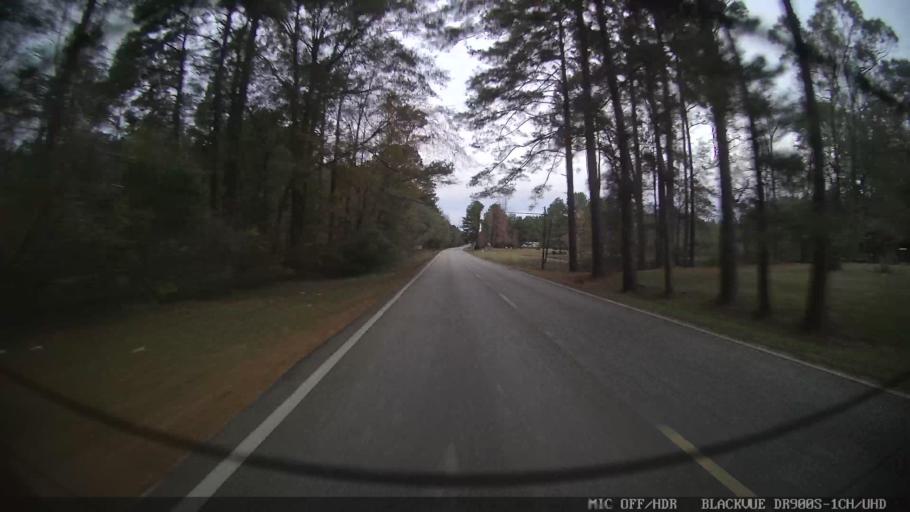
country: US
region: Mississippi
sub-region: Clarke County
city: Stonewall
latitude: 32.0481
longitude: -88.8937
